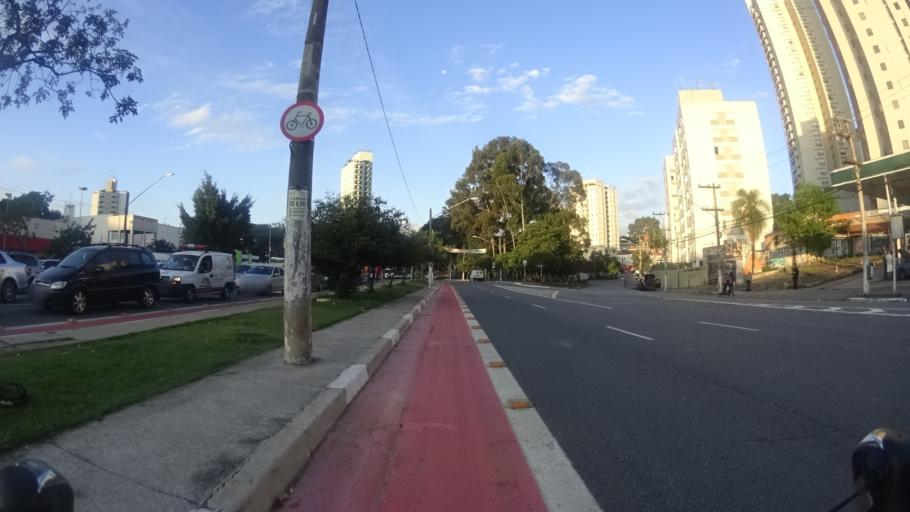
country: BR
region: Sao Paulo
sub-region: Sao Paulo
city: Sao Paulo
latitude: -23.4828
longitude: -46.6315
